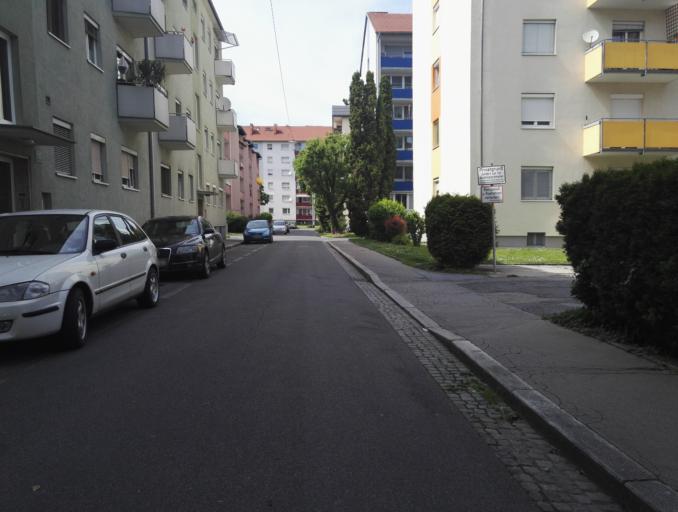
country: AT
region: Styria
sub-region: Graz Stadt
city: Graz
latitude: 47.0542
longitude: 15.4410
